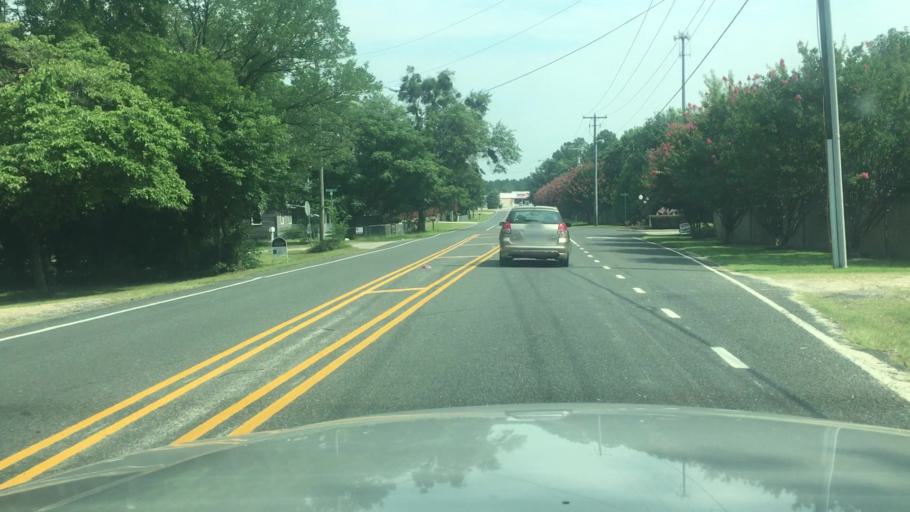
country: US
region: North Carolina
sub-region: Cumberland County
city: Hope Mills
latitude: 35.0036
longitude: -78.9649
